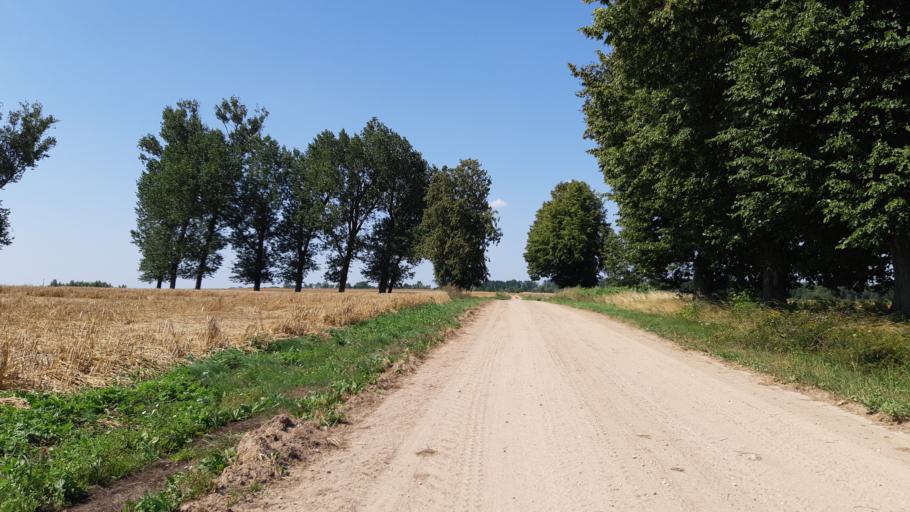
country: LT
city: Virbalis
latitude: 54.6390
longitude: 22.8220
